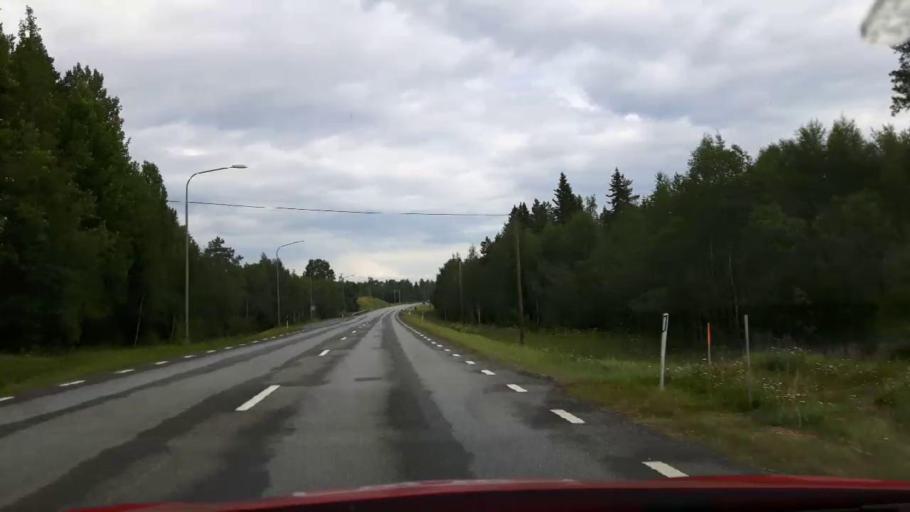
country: SE
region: Jaemtland
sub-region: Stroemsunds Kommun
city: Stroemsund
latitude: 63.6782
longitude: 15.3984
